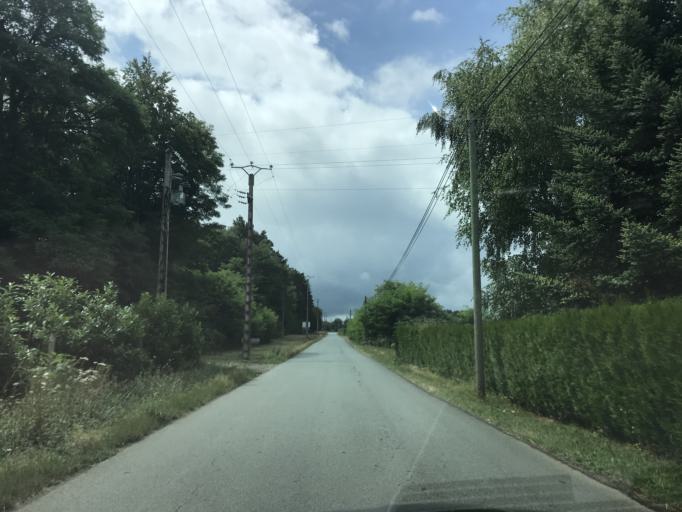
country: FR
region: Auvergne
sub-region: Departement du Cantal
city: Pleaux
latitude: 45.2633
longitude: 2.2031
